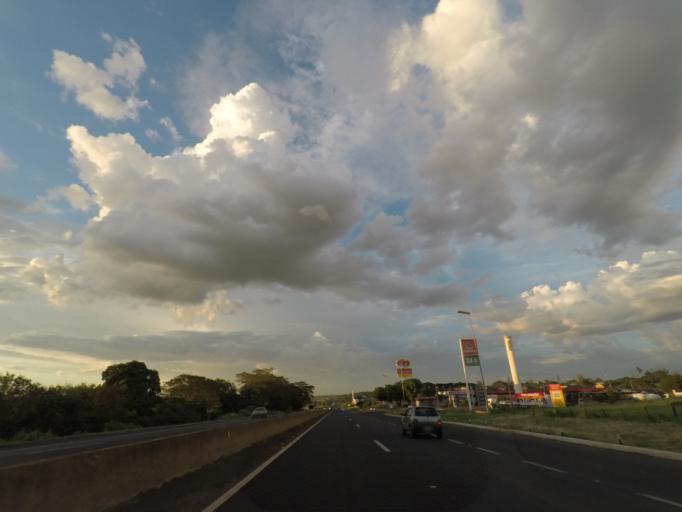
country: BR
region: Minas Gerais
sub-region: Uberaba
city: Uberaba
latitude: -19.7664
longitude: -47.9755
